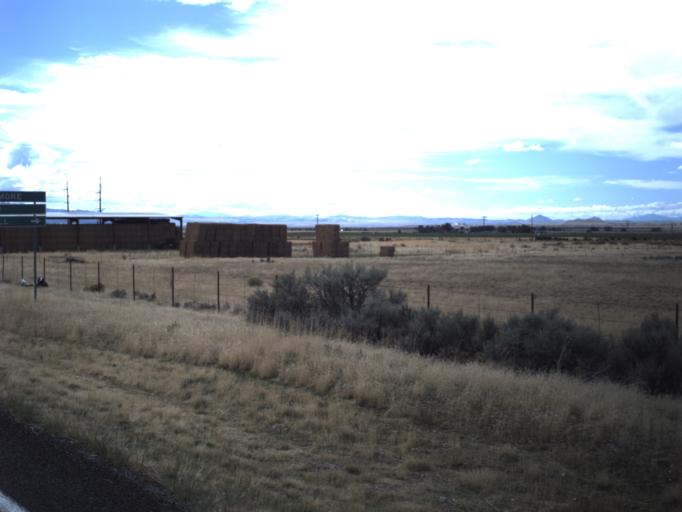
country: US
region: Utah
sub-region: Millard County
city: Fillmore
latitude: 38.9816
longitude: -112.4099
